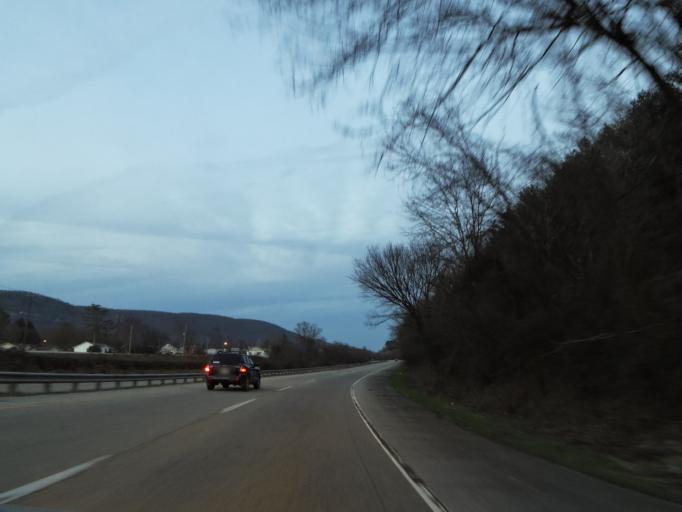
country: US
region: Tennessee
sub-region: Roane County
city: Harriman
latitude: 35.9540
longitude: -84.5334
